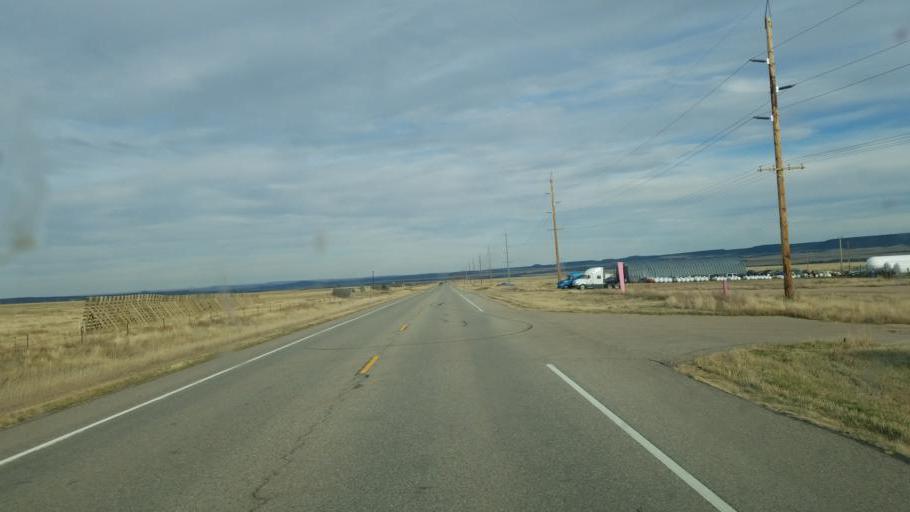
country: US
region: Colorado
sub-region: Huerfano County
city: Walsenburg
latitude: 37.5426
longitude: -105.0375
